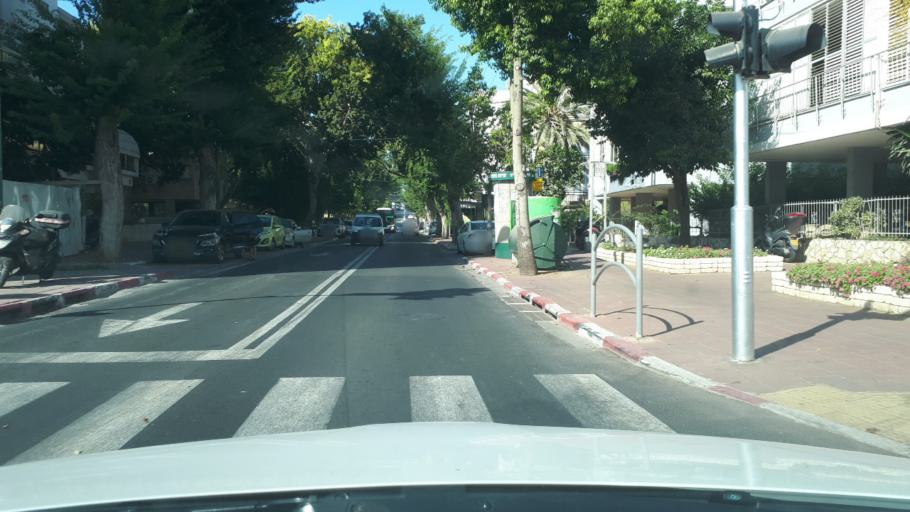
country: IL
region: Tel Aviv
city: Giv`atayim
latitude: 32.0640
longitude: 34.8236
